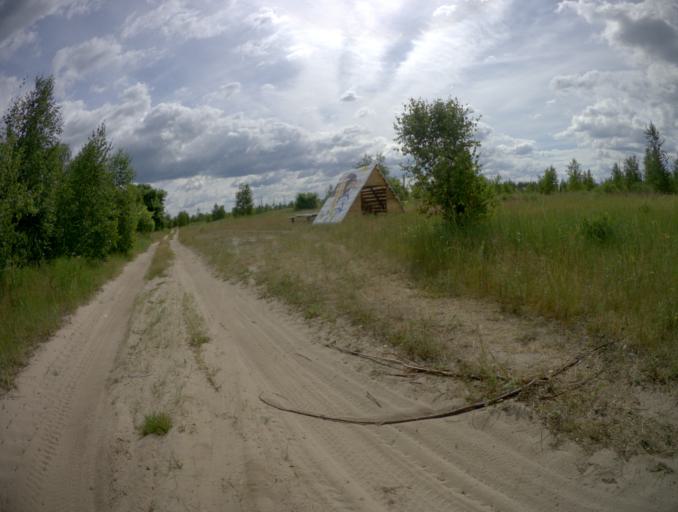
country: RU
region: Ivanovo
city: Talitsy
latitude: 56.5139
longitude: 42.4923
